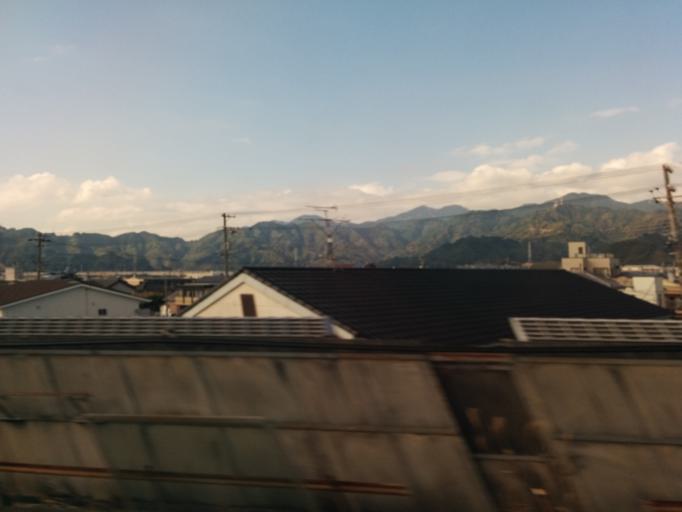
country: JP
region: Shizuoka
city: Shizuoka-shi
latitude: 35.0300
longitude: 138.4771
